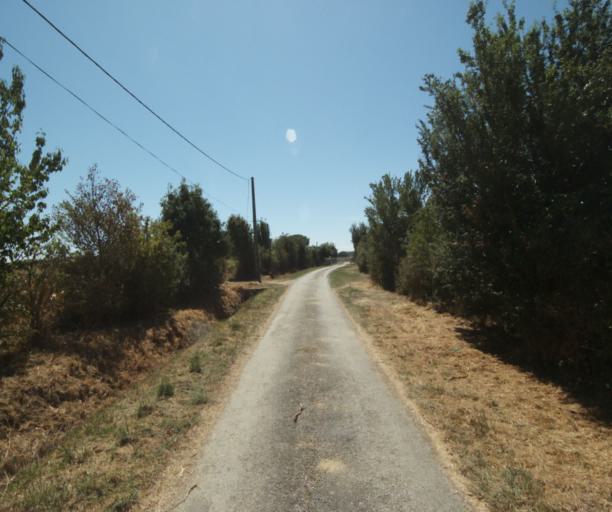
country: FR
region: Midi-Pyrenees
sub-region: Departement de la Haute-Garonne
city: Saint-Felix-Lauragais
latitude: 43.4698
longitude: 1.9416
